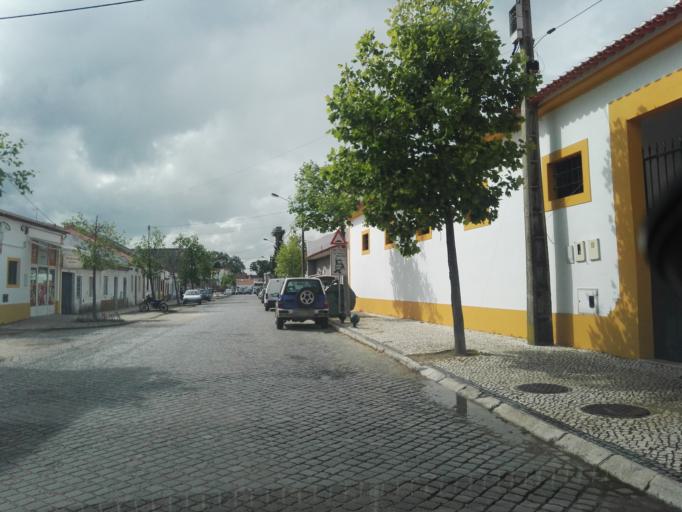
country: PT
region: Santarem
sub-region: Golega
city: Golega
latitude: 39.4057
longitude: -8.4831
